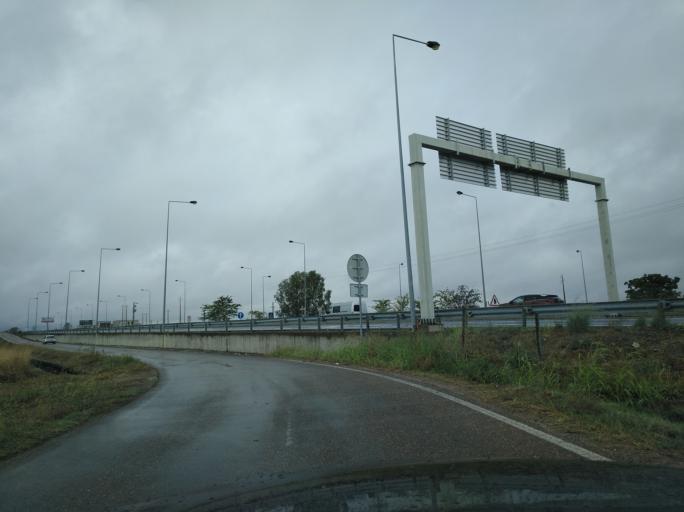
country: ES
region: Extremadura
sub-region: Provincia de Badajoz
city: Badajoz
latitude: 38.8836
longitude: -7.0534
